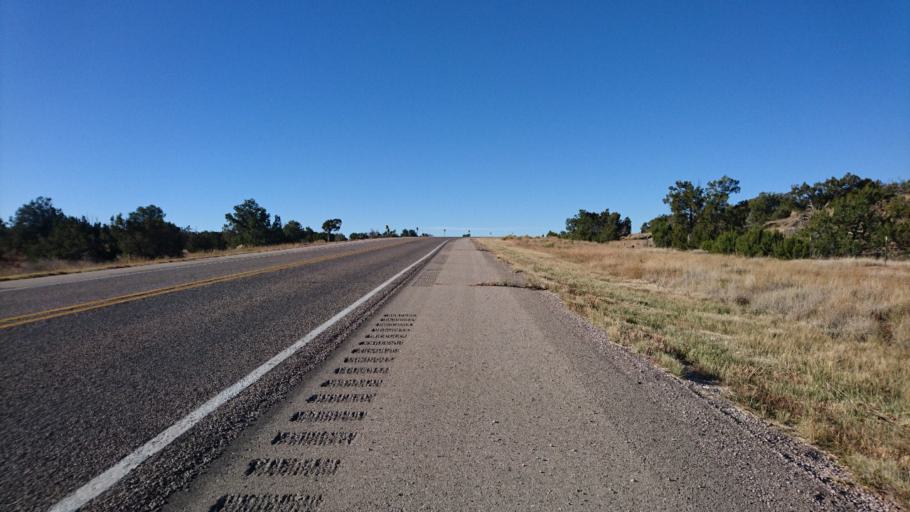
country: US
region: New Mexico
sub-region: Cibola County
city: Grants
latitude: 34.9639
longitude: -107.9141
